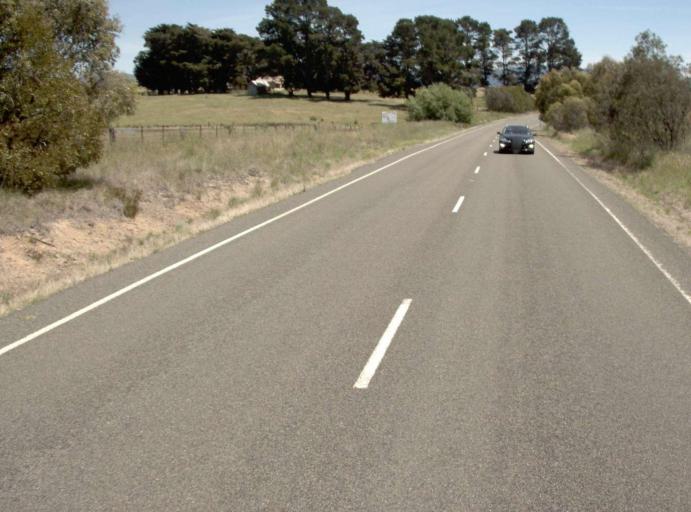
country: AU
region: Victoria
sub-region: Alpine
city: Mount Beauty
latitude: -37.1508
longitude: 147.6501
